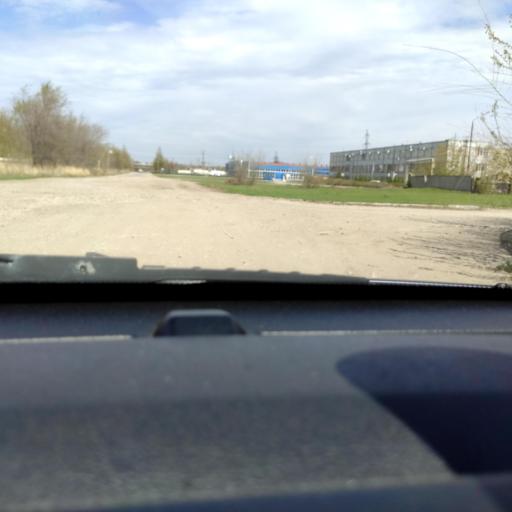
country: RU
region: Samara
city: Podstepki
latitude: 53.5771
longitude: 49.2280
